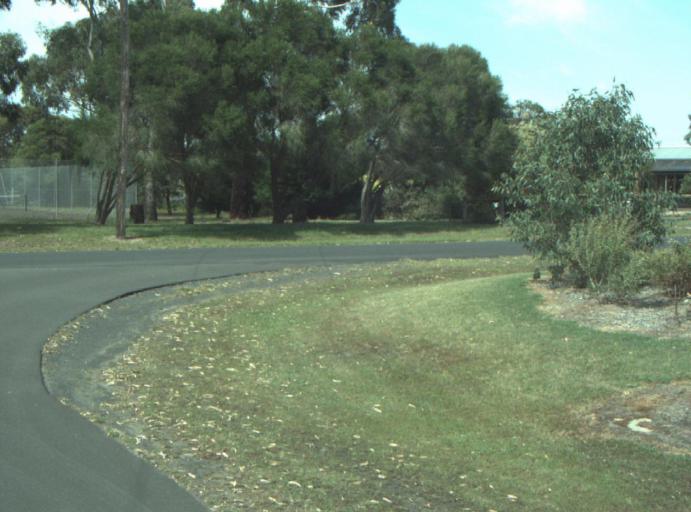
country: AU
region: Victoria
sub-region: Greater Geelong
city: Clifton Springs
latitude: -38.1813
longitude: 144.5752
